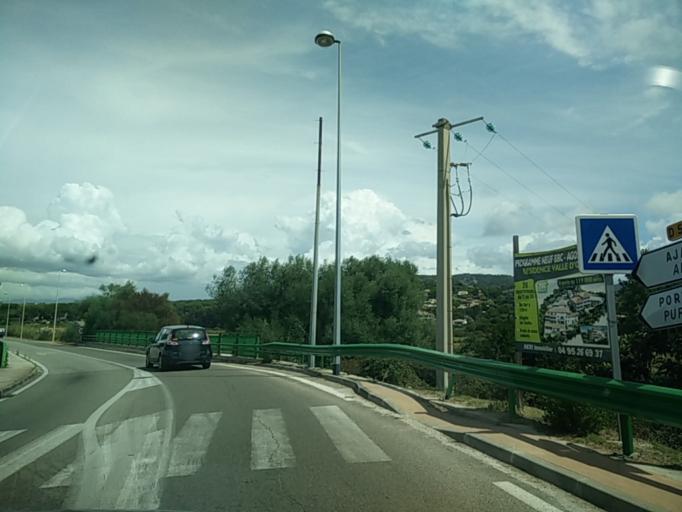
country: FR
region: Corsica
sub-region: Departement de la Corse-du-Sud
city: Pietrosella
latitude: 41.8514
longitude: 8.7906
